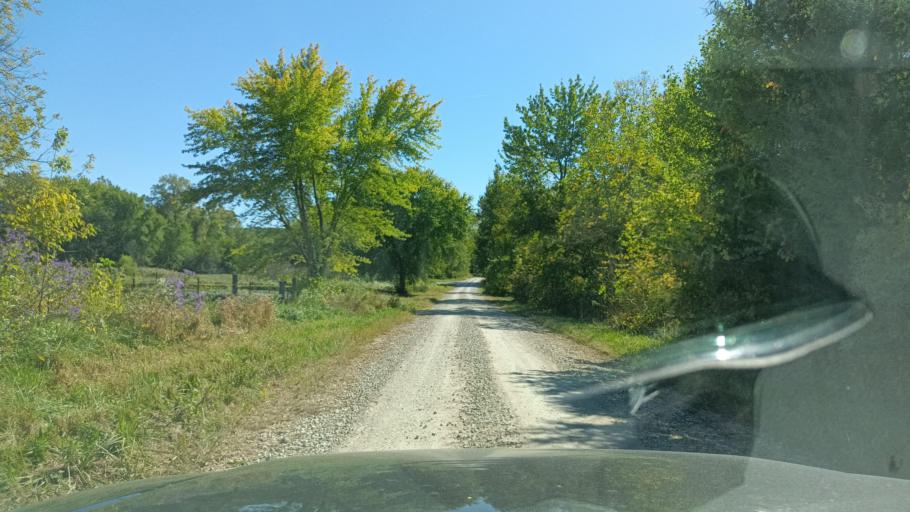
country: US
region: Missouri
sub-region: Macon County
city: La Plata
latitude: 39.9674
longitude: -92.6434
